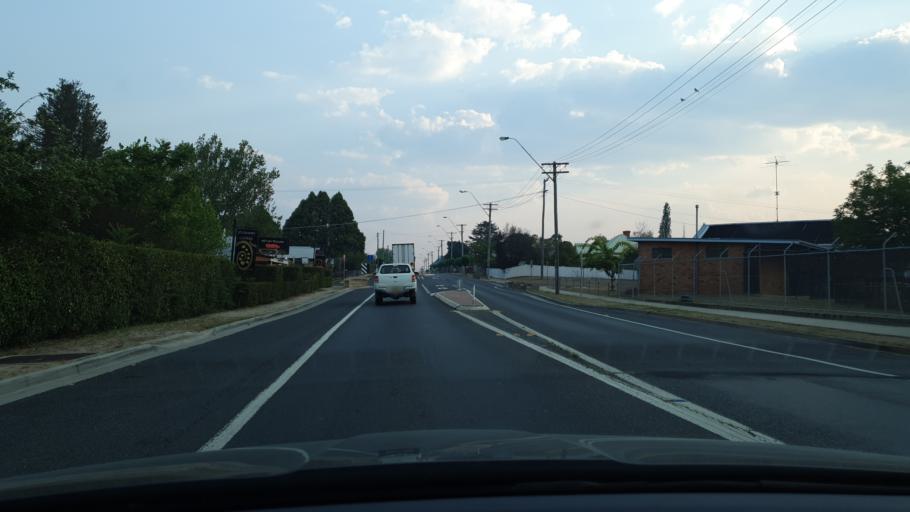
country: AU
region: New South Wales
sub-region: Tenterfield Municipality
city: Carrolls Creek
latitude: -29.0469
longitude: 152.0204
